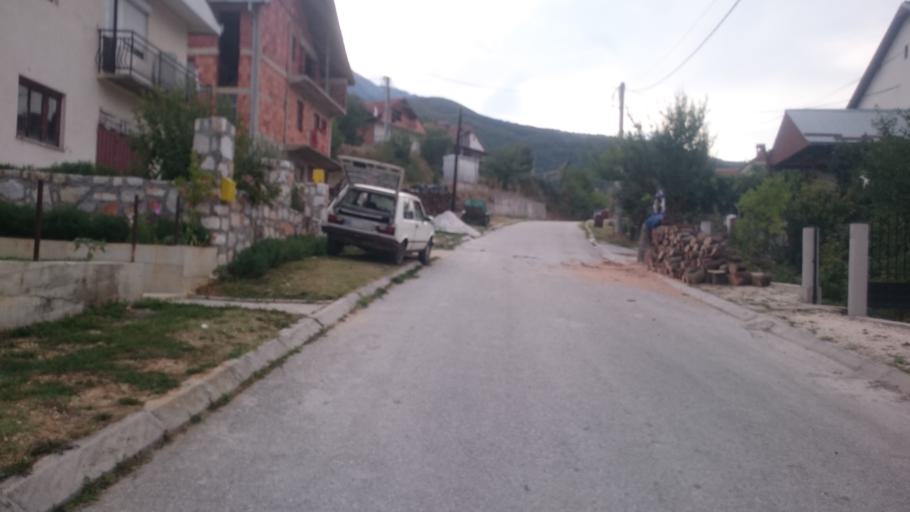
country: MK
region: Makedonski Brod
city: Makedonski Brod
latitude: 41.5168
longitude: 21.2166
